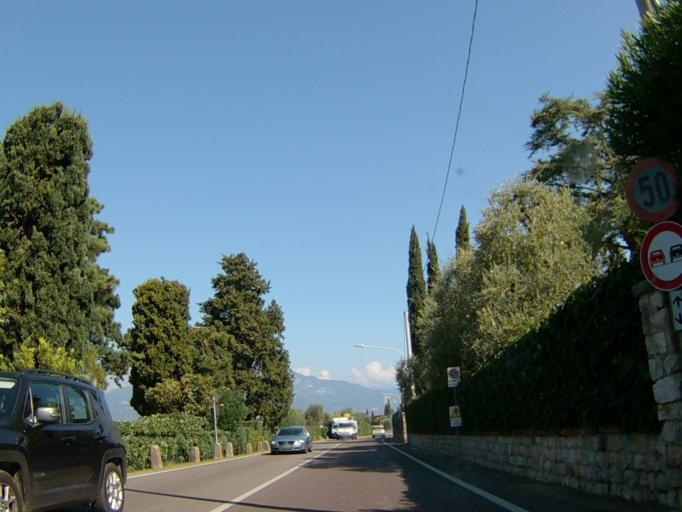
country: IT
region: Veneto
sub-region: Provincia di Verona
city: Torri del Benaco
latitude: 45.6013
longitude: 10.6855
